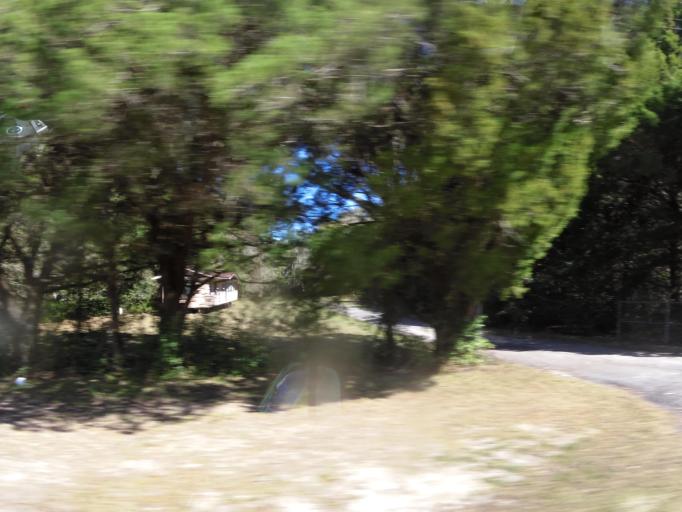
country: US
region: Florida
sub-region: Clay County
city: Green Cove Springs
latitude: 29.8680
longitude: -81.6819
